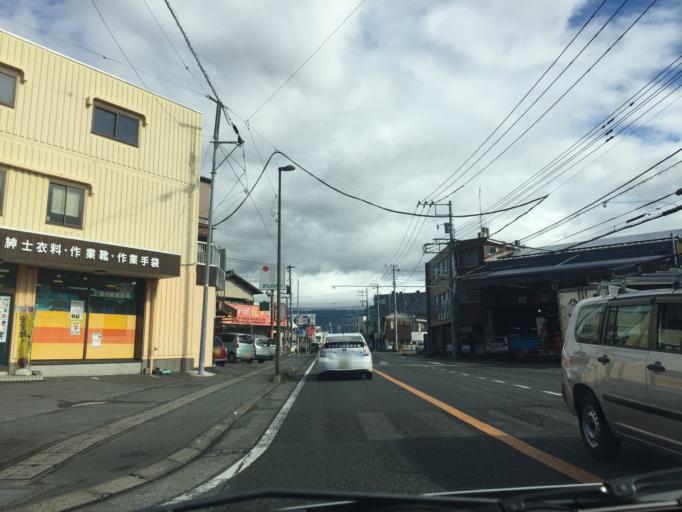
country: JP
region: Shizuoka
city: Mishima
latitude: 35.1135
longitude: 138.8983
